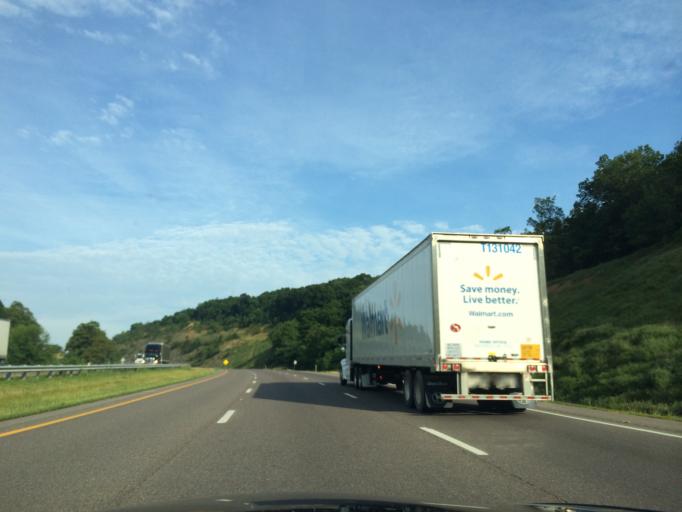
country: US
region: Maryland
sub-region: Allegany County
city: Cumberland
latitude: 39.6966
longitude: -78.5148
